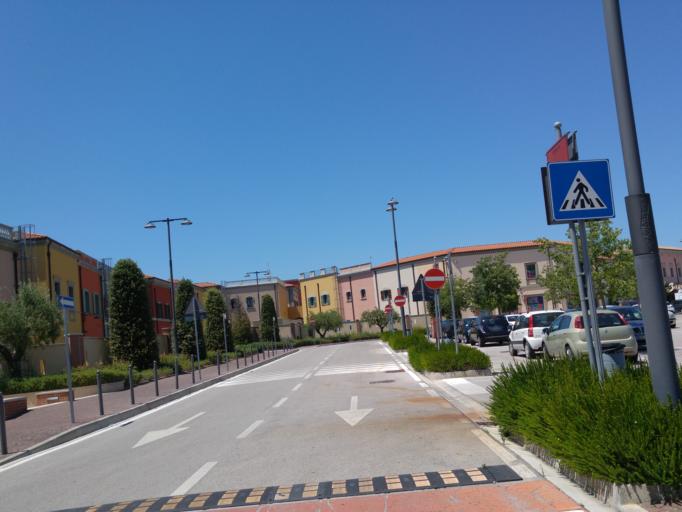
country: IT
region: Abruzzo
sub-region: Provincia di Pescara
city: San Martino Bassa
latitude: 42.5133
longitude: 14.1194
